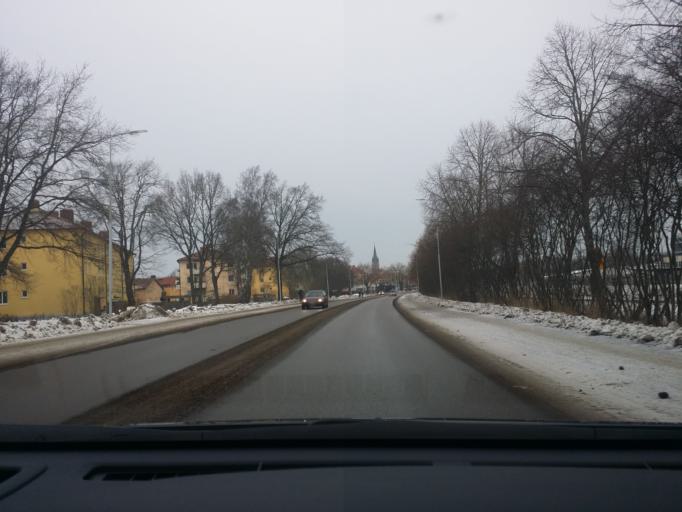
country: SE
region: Vaestra Goetaland
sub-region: Mariestads Kommun
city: Mariestad
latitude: 58.7022
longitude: 13.8203
